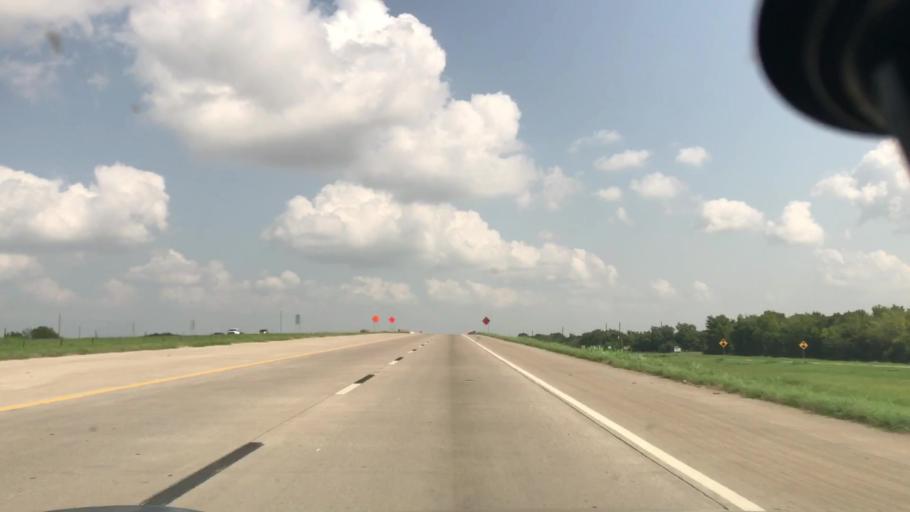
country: US
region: Texas
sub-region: Brazoria County
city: Iowa Colony
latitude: 29.5092
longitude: -95.3875
